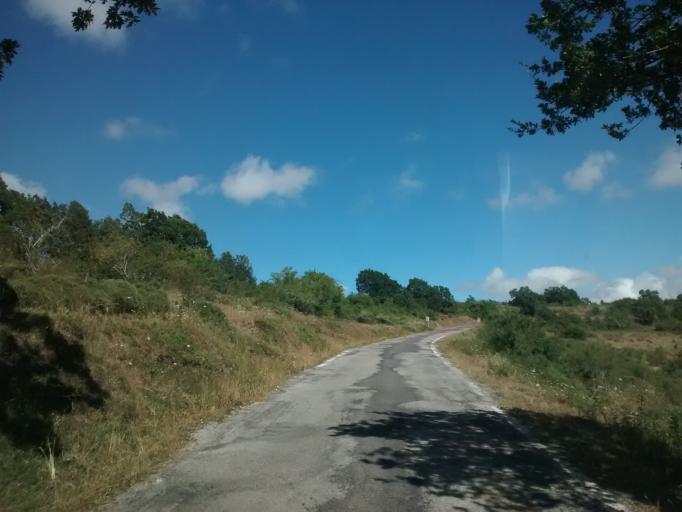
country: ES
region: Castille and Leon
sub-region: Provincia de Palencia
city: Berzosilla
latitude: 42.8701
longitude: -4.0550
